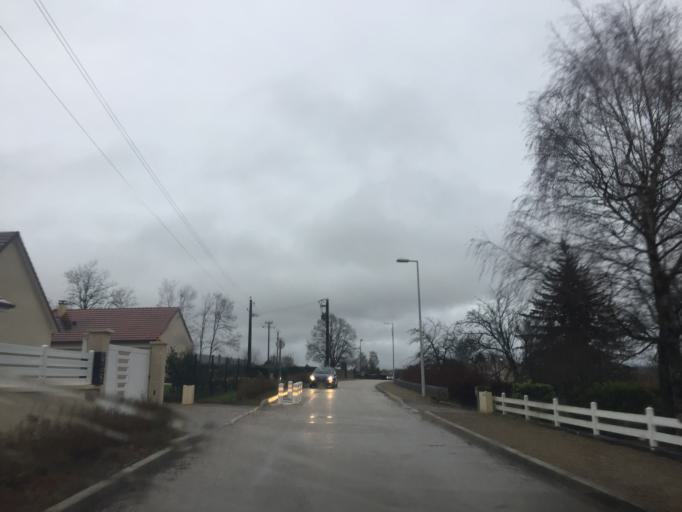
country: FR
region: Franche-Comte
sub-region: Departement du Jura
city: Dole
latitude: 47.0979
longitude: 5.5270
